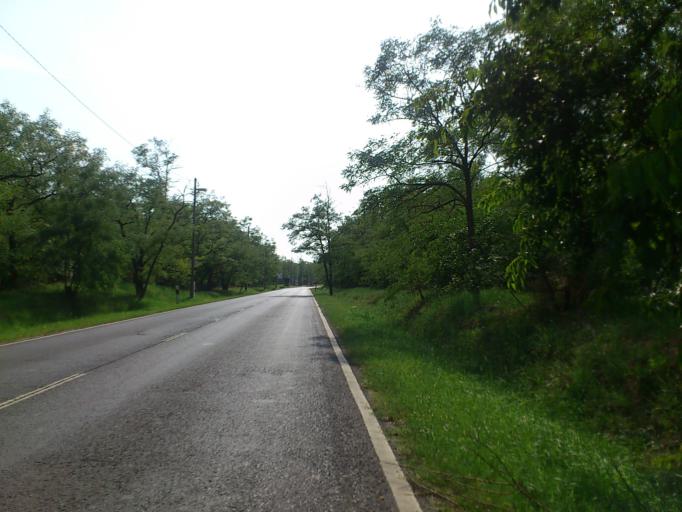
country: HU
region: Budapest
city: Budapest XVII. keruelet
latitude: 47.4547
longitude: 19.2308
